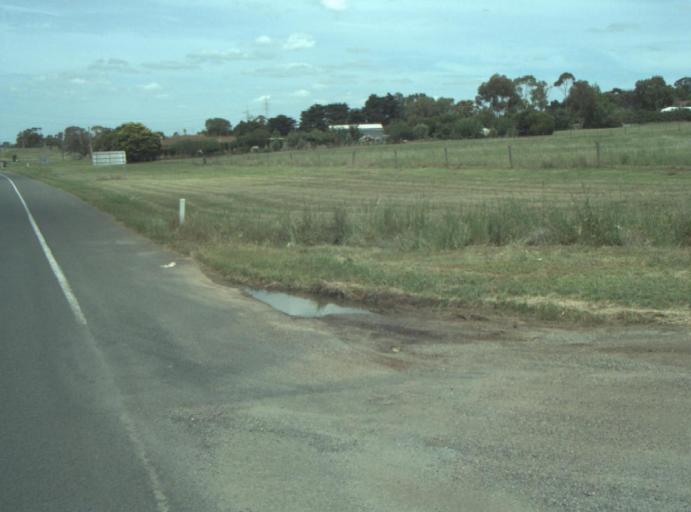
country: AU
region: Victoria
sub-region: Greater Geelong
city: Lara
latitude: -38.0295
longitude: 144.3543
